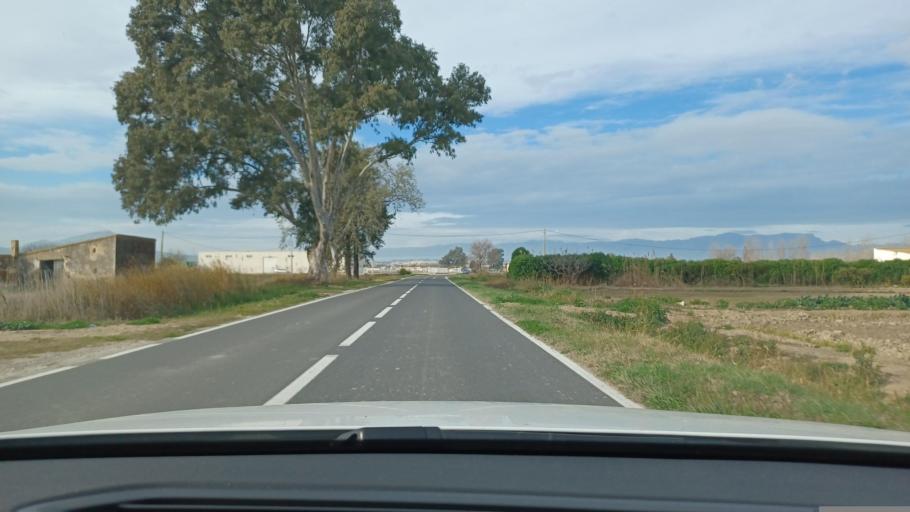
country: ES
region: Catalonia
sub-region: Provincia de Tarragona
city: Amposta
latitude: 40.7027
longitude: 0.6147
